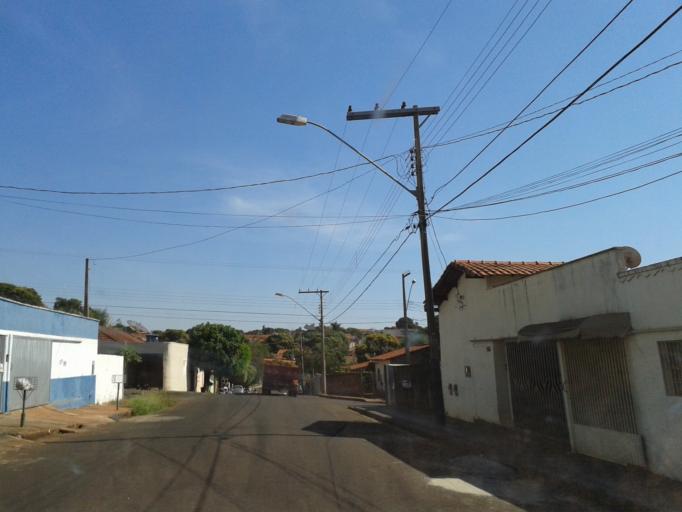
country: BR
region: Minas Gerais
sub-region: Ituiutaba
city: Ituiutaba
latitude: -18.9804
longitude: -49.4713
